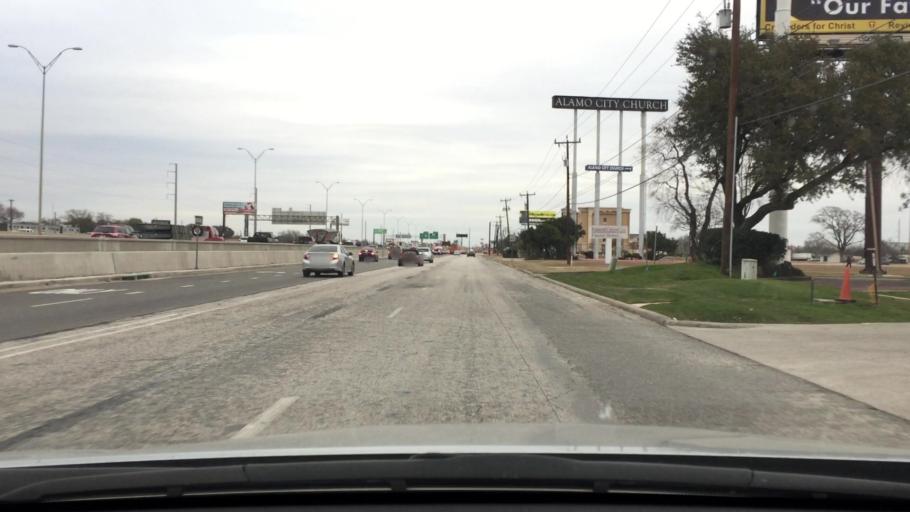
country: US
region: Texas
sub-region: Bexar County
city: Kirby
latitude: 29.4886
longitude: -98.4018
